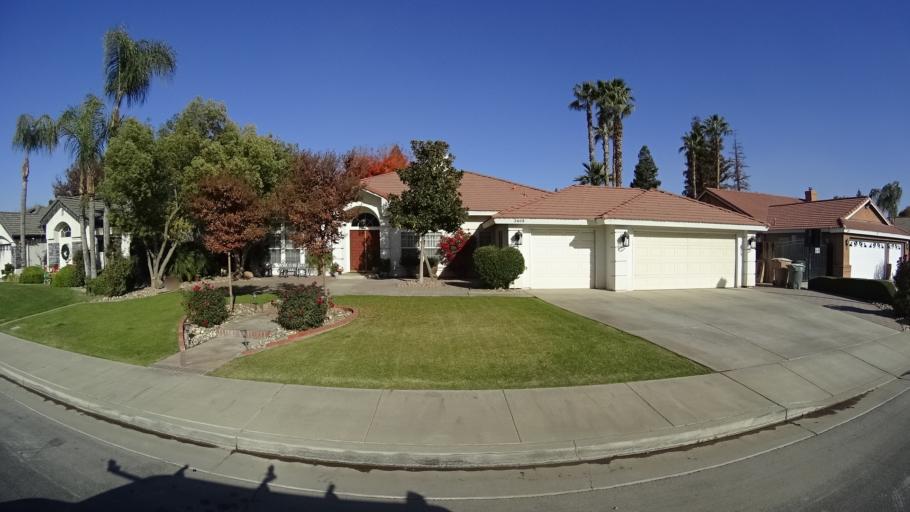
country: US
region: California
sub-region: Kern County
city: Greenfield
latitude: 35.2760
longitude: -119.0409
